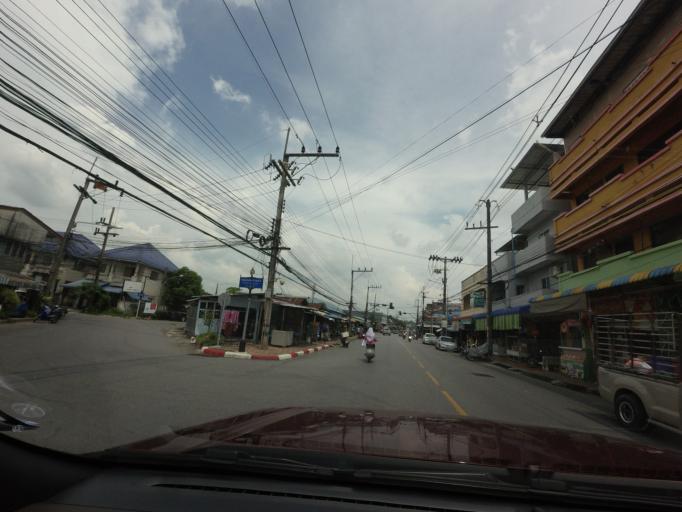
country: TH
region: Yala
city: Yala
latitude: 6.5347
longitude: 101.2863
